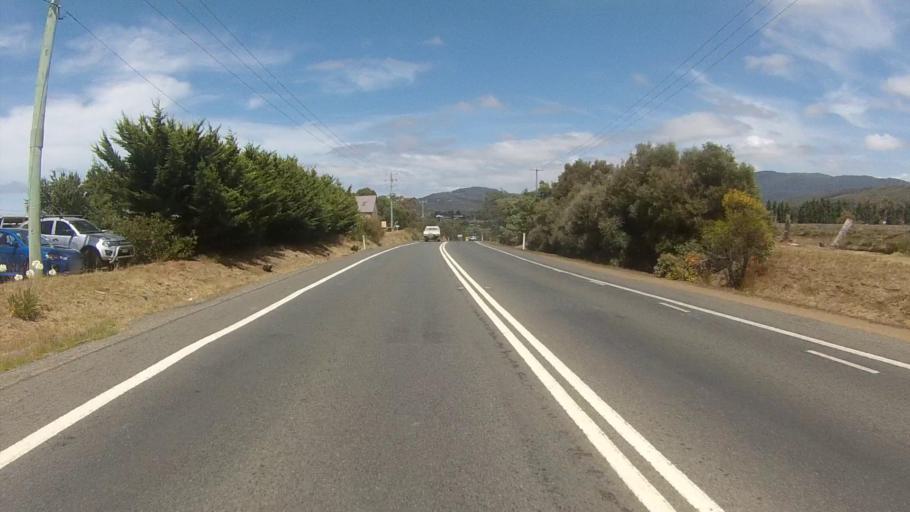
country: AU
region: Tasmania
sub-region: Kingborough
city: Margate
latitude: -43.0177
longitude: 147.2702
